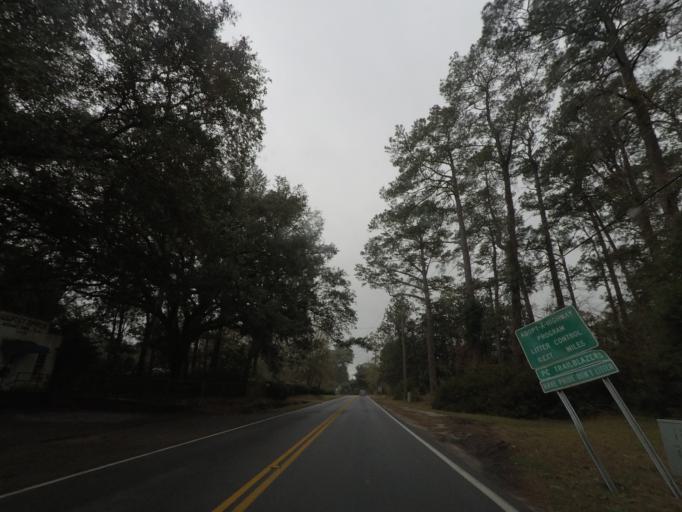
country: US
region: South Carolina
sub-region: Charleston County
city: Ravenel
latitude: 32.7203
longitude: -80.3484
